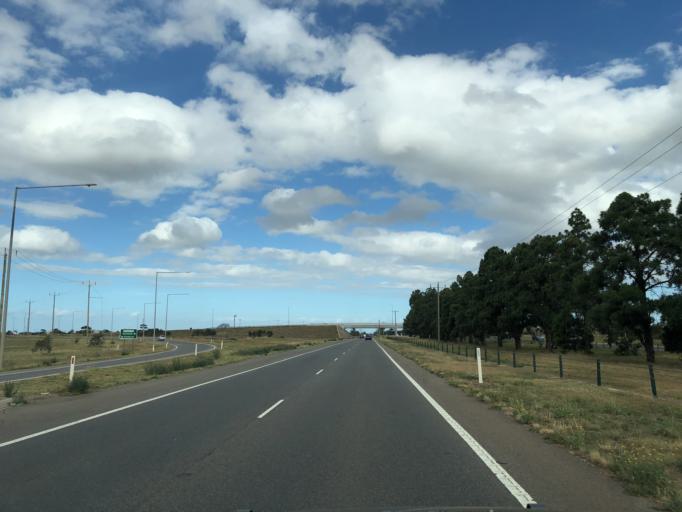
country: AU
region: Victoria
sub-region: Melton
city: Rockbank
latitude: -37.7210
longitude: 144.6478
